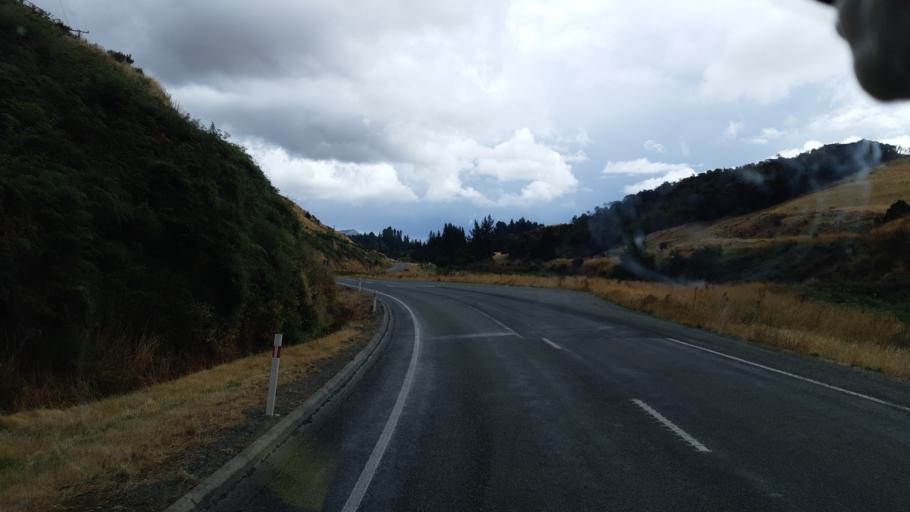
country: NZ
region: Canterbury
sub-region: Hurunui District
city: Amberley
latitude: -42.5951
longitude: 172.5362
